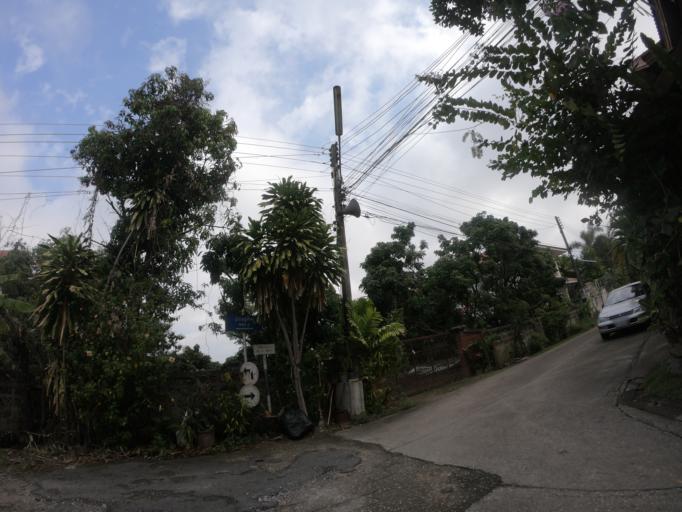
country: TH
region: Chiang Mai
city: Chiang Mai
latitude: 18.7588
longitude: 98.9741
